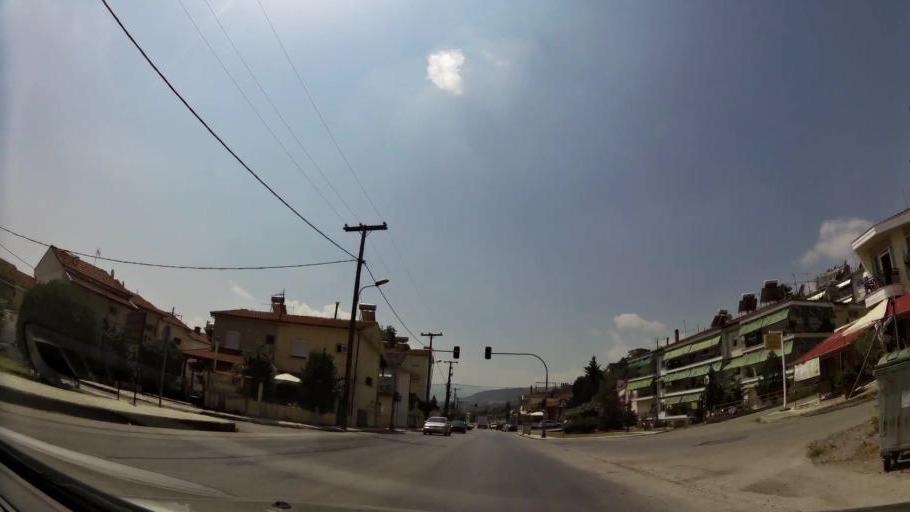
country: GR
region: Central Macedonia
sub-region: Nomos Imathias
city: Veroia
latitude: 40.5305
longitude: 22.2079
